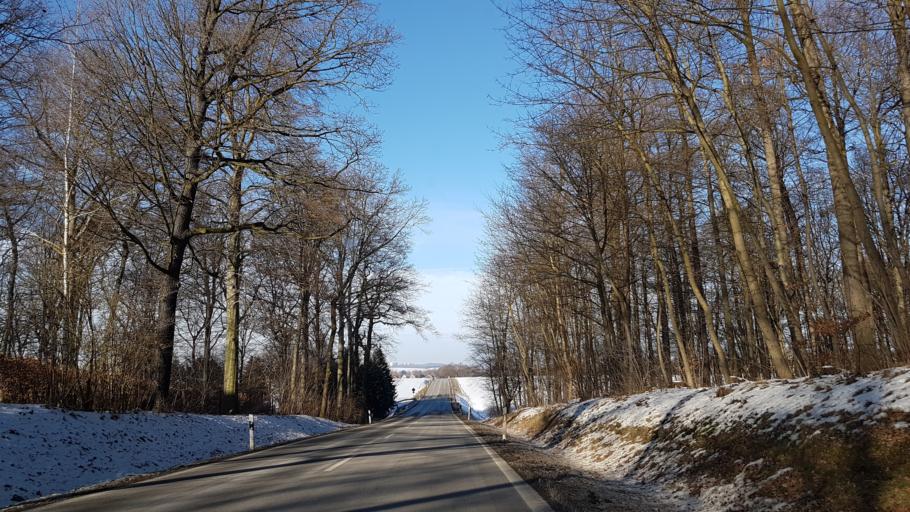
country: DE
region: Thuringia
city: Nobitz
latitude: 50.9615
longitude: 12.5059
